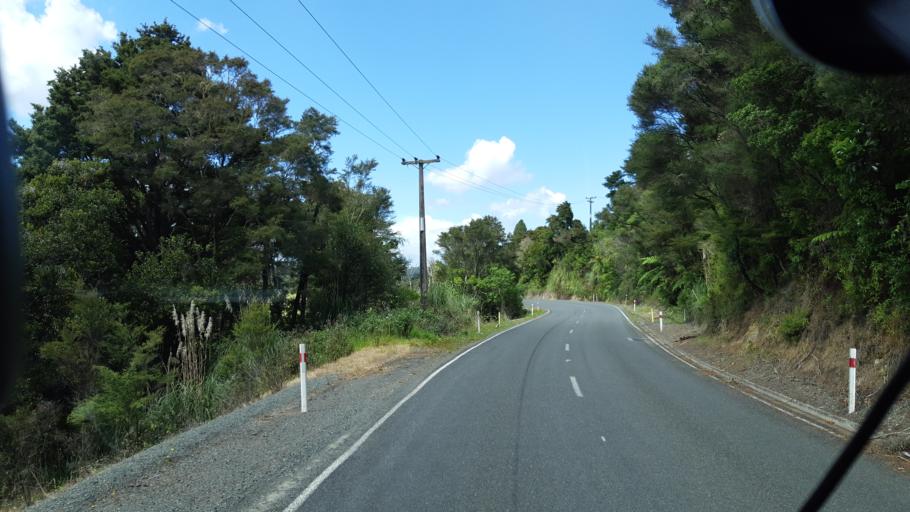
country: NZ
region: Northland
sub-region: Far North District
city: Taipa
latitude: -35.2547
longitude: 173.5349
